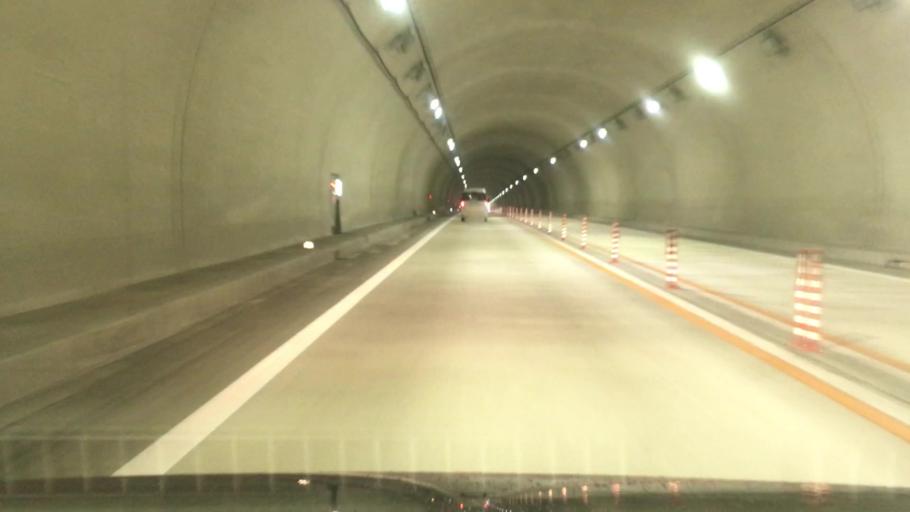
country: JP
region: Hyogo
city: Toyooka
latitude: 35.4440
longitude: 134.7669
